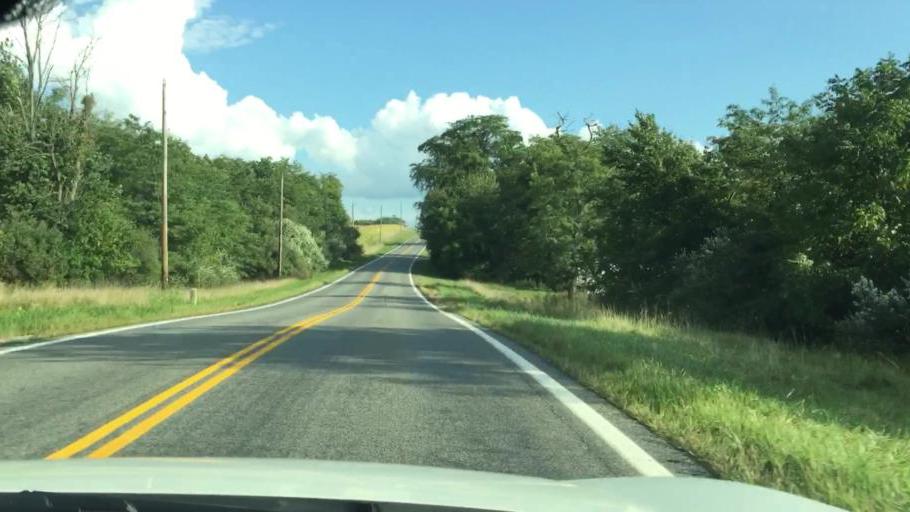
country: US
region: Ohio
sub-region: Champaign County
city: Mechanicsburg
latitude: 40.0384
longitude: -83.6041
